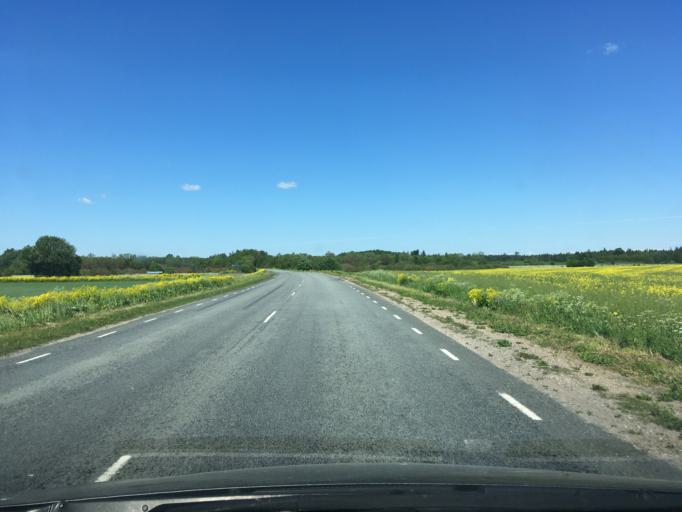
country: EE
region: Harju
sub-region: Rae vald
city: Vaida
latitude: 59.1877
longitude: 25.0082
